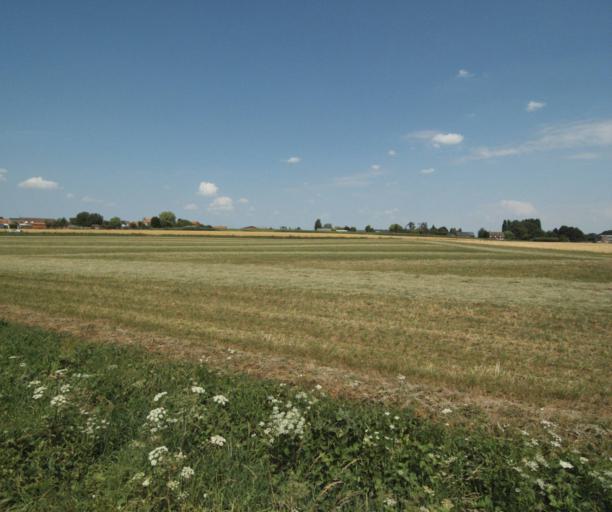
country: FR
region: Nord-Pas-de-Calais
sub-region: Departement du Nord
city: Neuville-en-Ferrain
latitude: 50.7532
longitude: 3.1760
